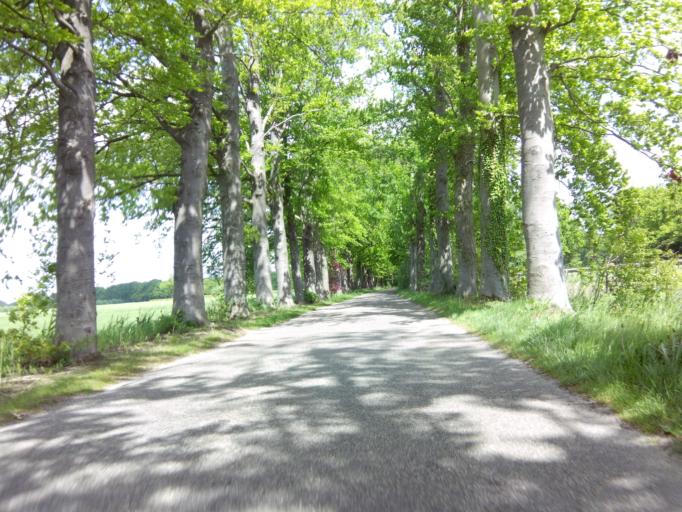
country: NL
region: Utrecht
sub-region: Gemeente Utrechtse Heuvelrug
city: Overberg
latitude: 52.0657
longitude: 5.4724
